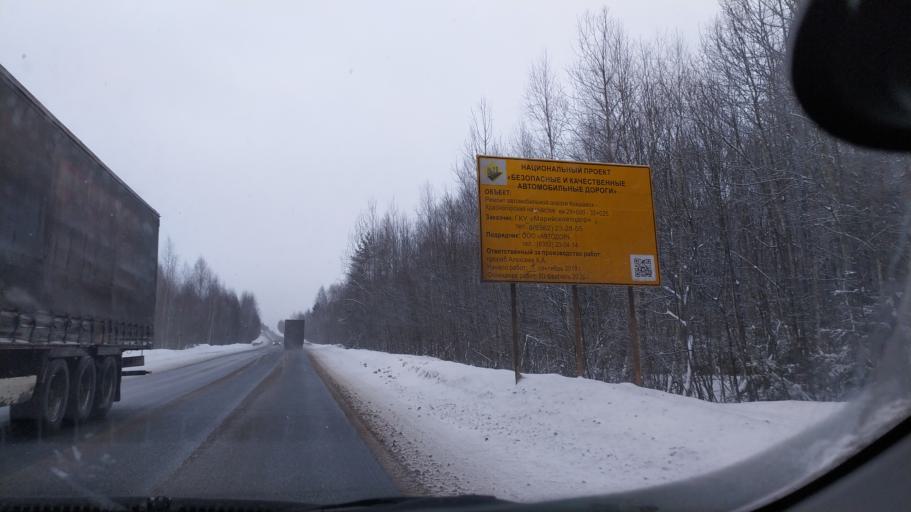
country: RU
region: Mariy-El
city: Krasnogorskiy
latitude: 56.1660
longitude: 48.2316
